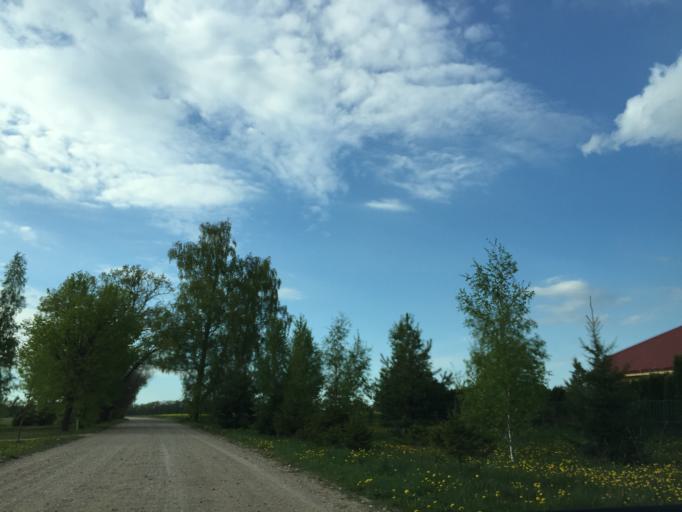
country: LV
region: Limbazu Rajons
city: Limbazi
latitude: 57.3700
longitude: 24.6909
